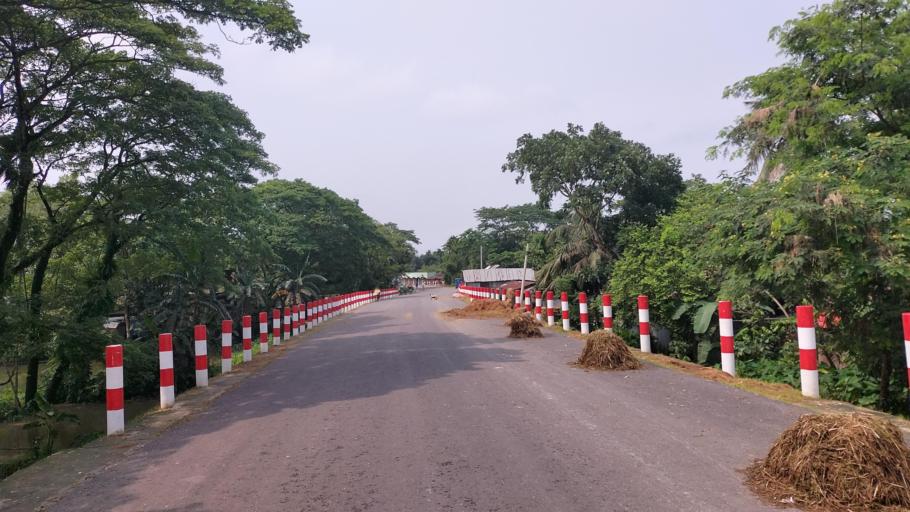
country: BD
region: Dhaka
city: Netrakona
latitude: 24.9558
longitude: 90.8346
